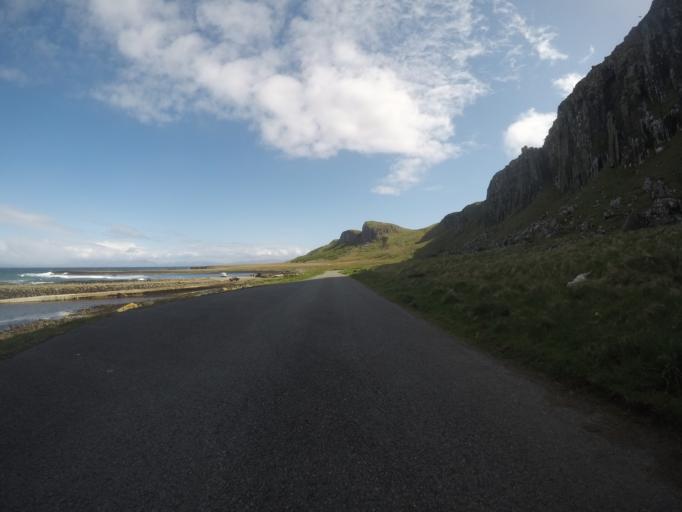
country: GB
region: Scotland
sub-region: Highland
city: Portree
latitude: 57.6338
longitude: -6.2008
